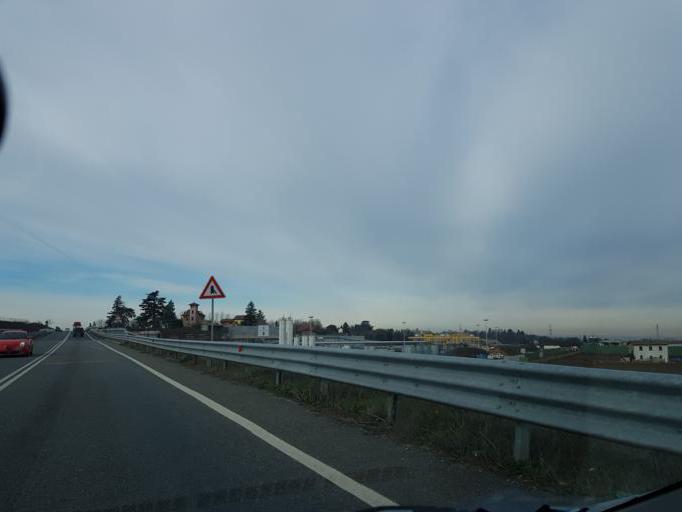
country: IT
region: Piedmont
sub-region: Provincia di Alessandria
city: Novi Ligure
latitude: 44.7573
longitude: 8.8176
